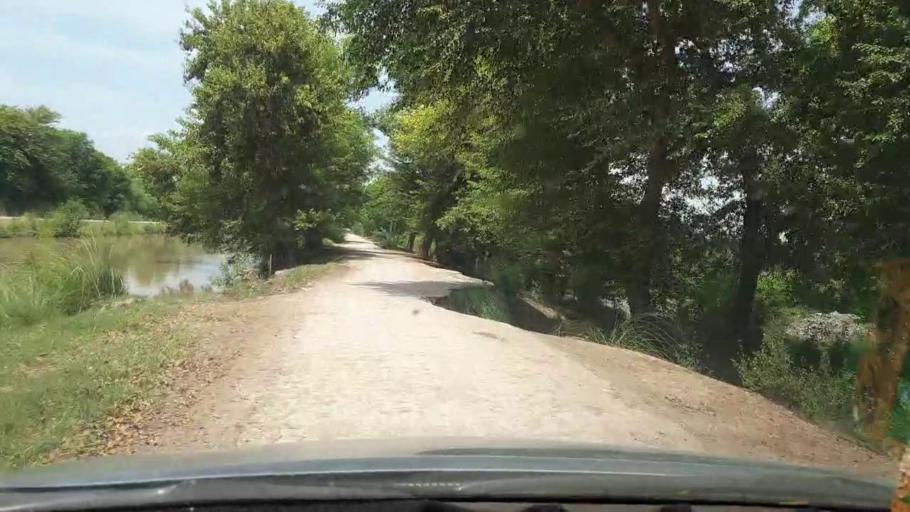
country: PK
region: Sindh
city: Khairpur
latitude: 27.4672
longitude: 68.8055
